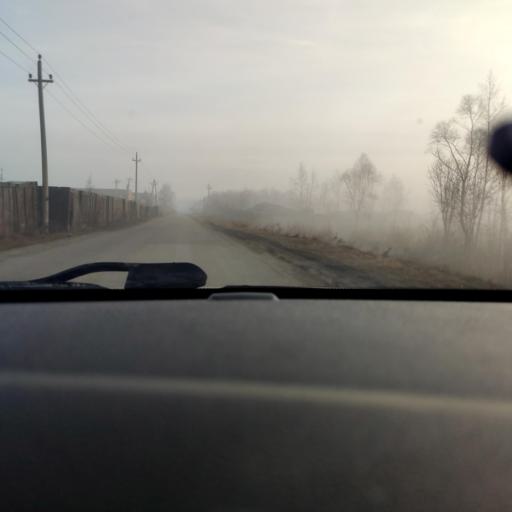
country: RU
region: Bashkortostan
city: Avdon
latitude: 54.6656
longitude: 55.8233
